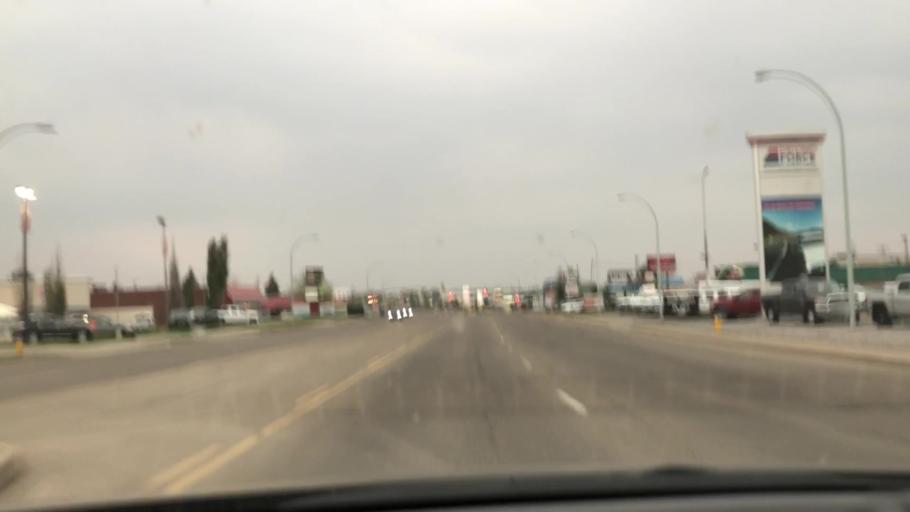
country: CA
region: Alberta
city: Edmonton
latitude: 53.4668
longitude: -113.4782
